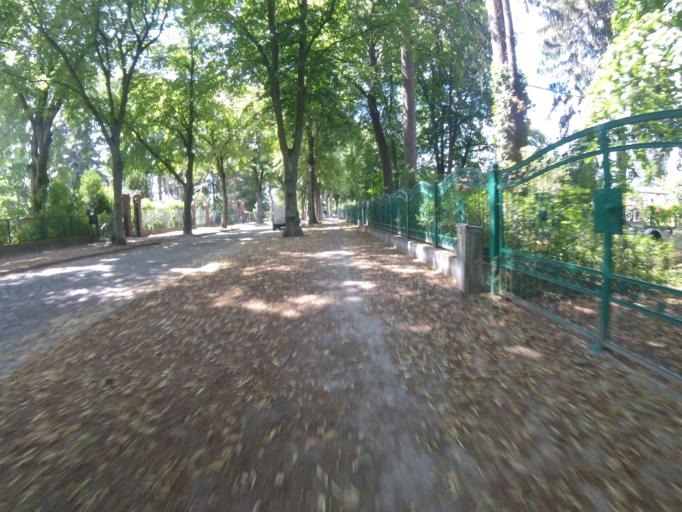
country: DE
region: Brandenburg
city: Wildau
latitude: 52.3359
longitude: 13.6462
